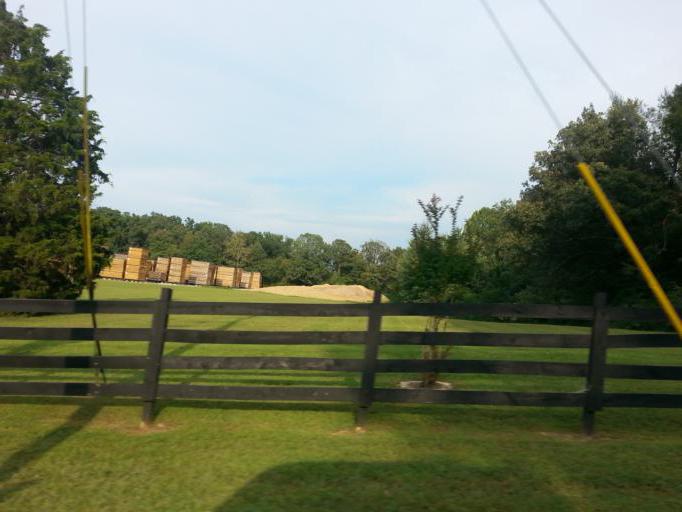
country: US
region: Tennessee
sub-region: Dickson County
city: Burns
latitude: 36.0215
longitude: -87.3324
